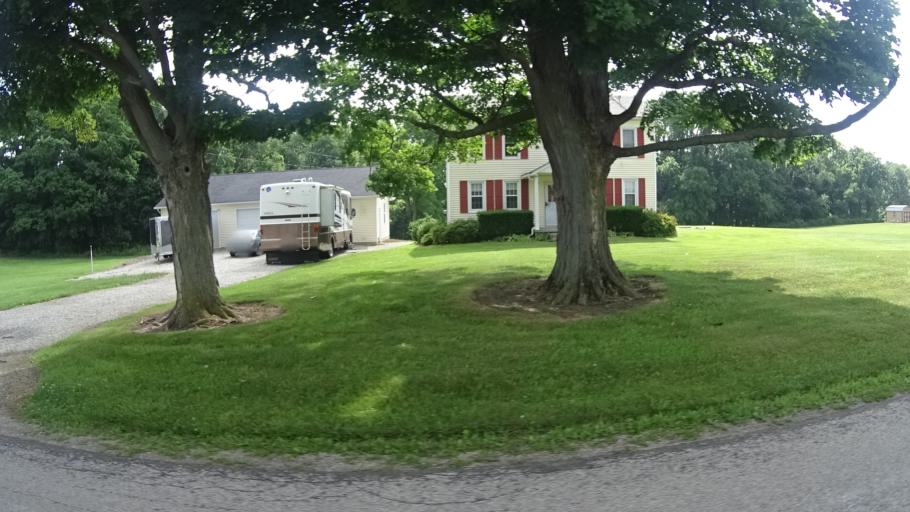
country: US
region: Ohio
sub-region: Huron County
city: Wakeman
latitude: 41.2904
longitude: -82.4201
